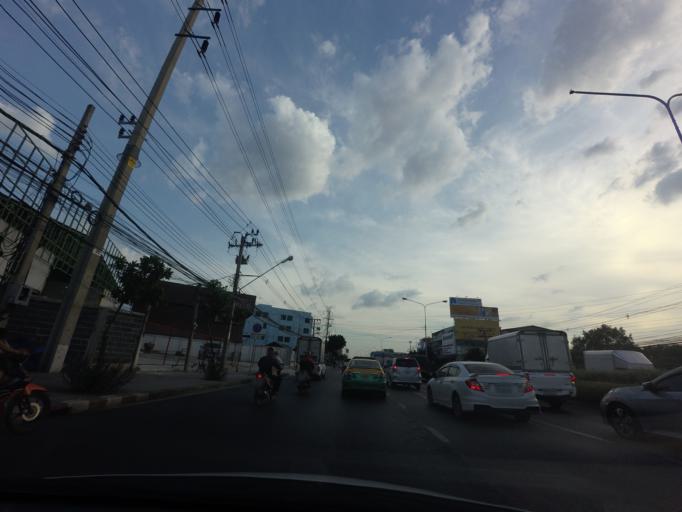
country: TH
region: Bangkok
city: Bang Khun Thian
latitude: 13.6503
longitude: 100.4311
